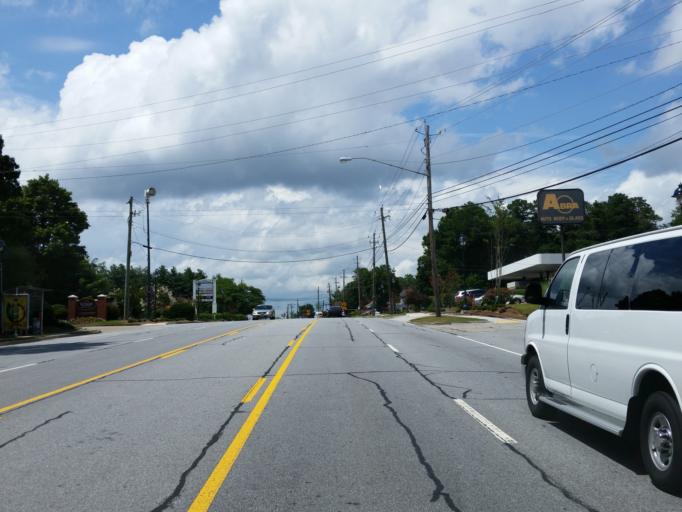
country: US
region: Georgia
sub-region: Fulton County
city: Roswell
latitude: 33.9853
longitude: -84.3506
